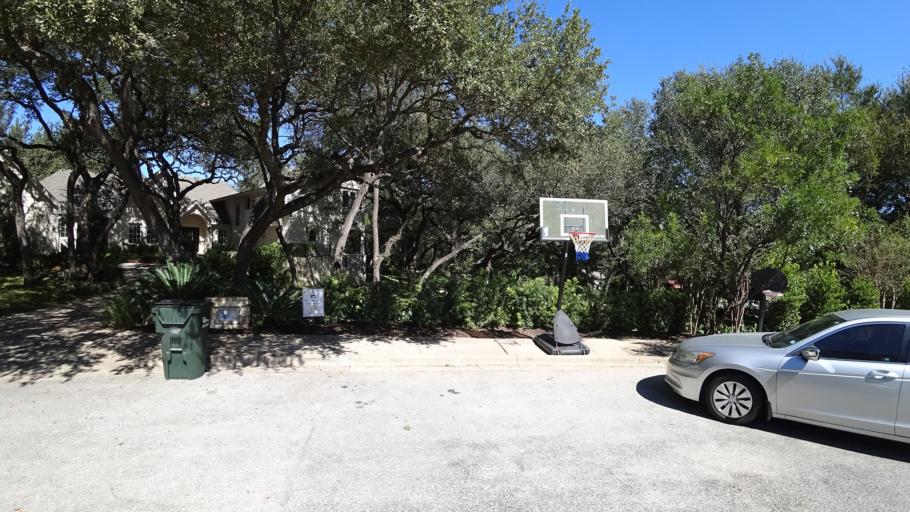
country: US
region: Texas
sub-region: Travis County
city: West Lake Hills
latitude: 30.3198
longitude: -97.7806
